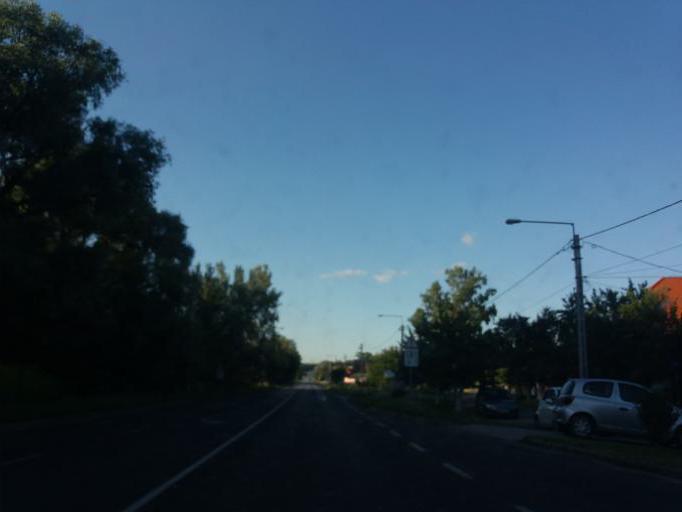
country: HU
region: Fejer
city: Baracska
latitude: 47.2860
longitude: 18.7561
